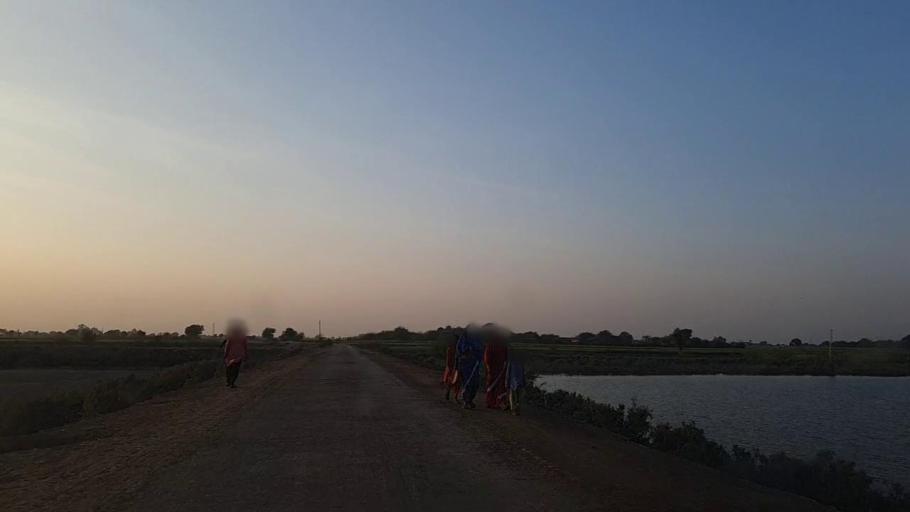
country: PK
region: Sindh
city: Naukot
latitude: 24.9458
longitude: 69.4431
